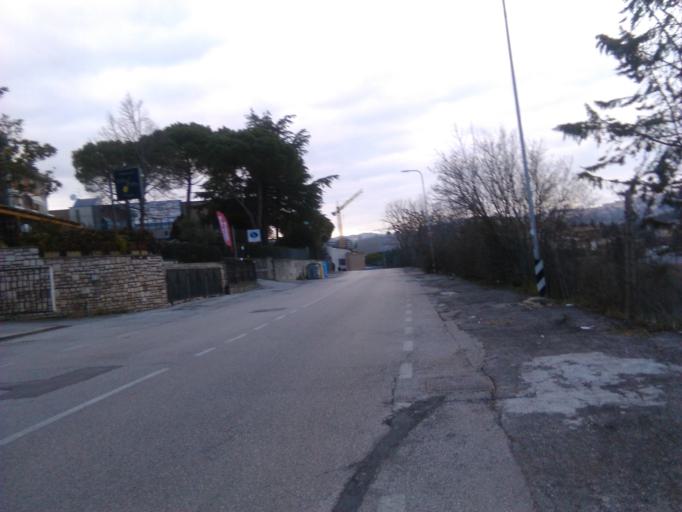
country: IT
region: Umbria
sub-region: Provincia di Perugia
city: Perugia
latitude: 43.0908
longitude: 12.3659
